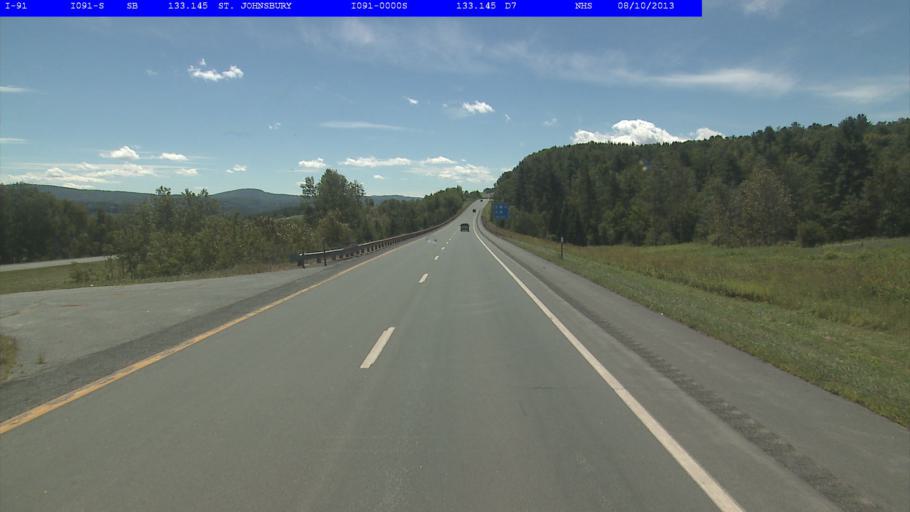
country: US
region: Vermont
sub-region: Caledonia County
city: St Johnsbury
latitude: 44.4624
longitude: -72.0245
